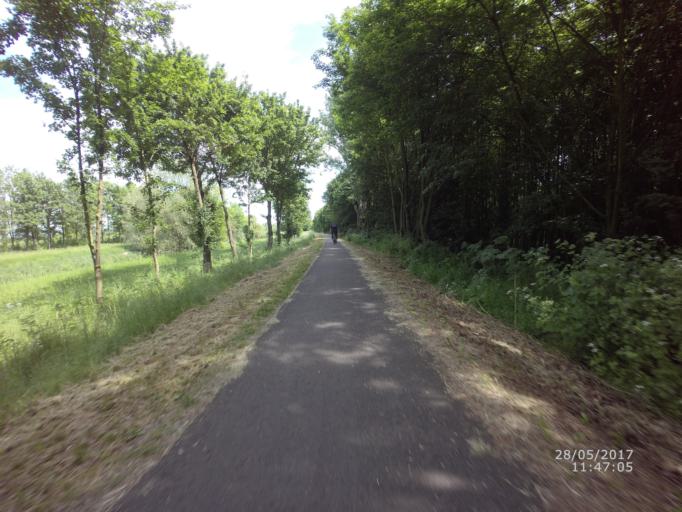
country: DE
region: Thuringia
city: Griefstedt
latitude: 51.1991
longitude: 11.1374
